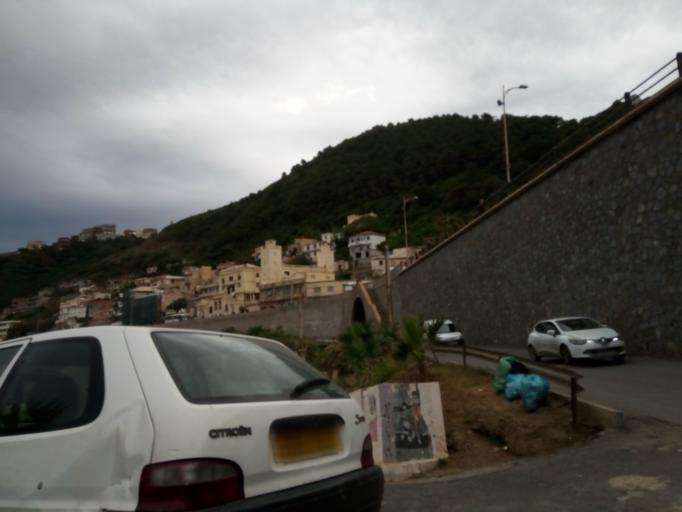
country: DZ
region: Alger
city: Algiers
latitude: 36.8130
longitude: 3.0215
